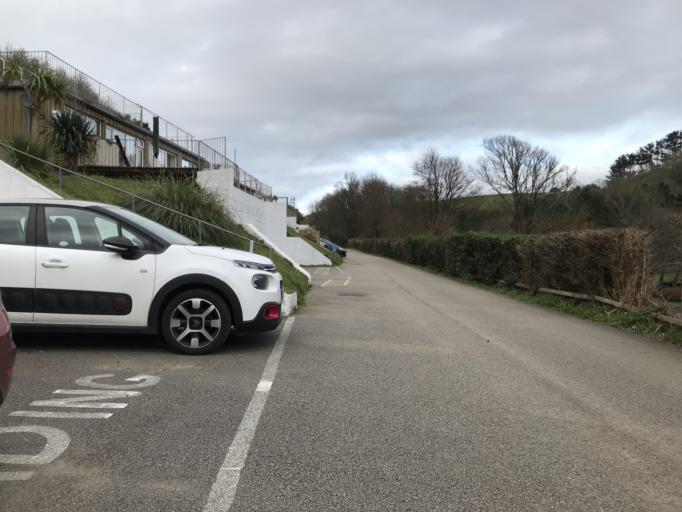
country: GB
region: England
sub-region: Cornwall
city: Looe
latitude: 50.3629
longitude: -4.4366
